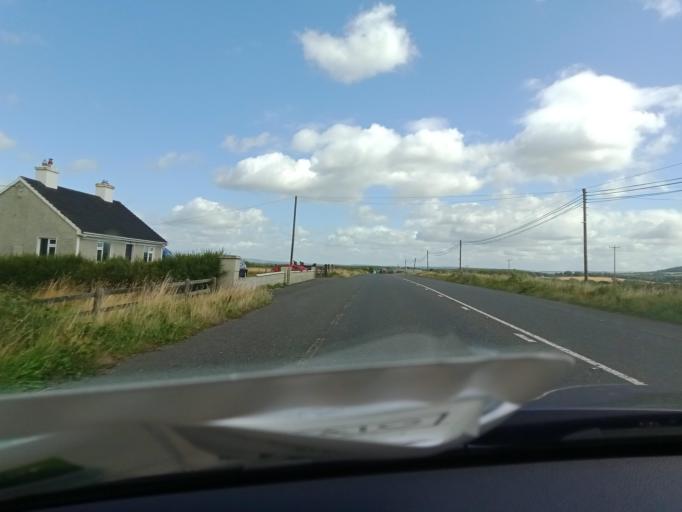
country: IE
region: Leinster
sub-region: Laois
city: Rathdowney
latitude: 52.8260
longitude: -7.4629
